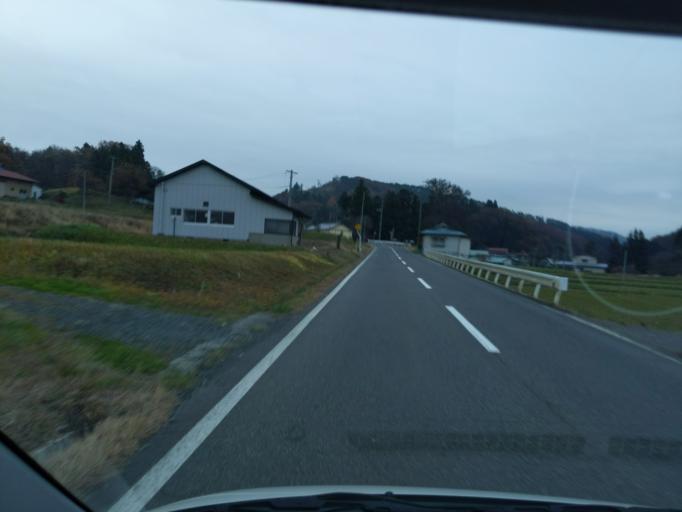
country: JP
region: Iwate
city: Kitakami
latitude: 39.2274
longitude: 141.2611
